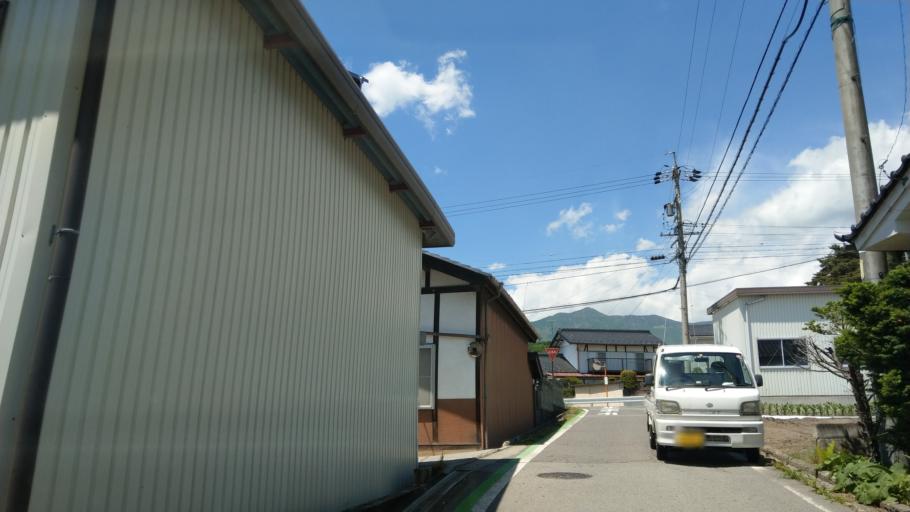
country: JP
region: Nagano
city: Komoro
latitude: 36.3328
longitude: 138.4546
